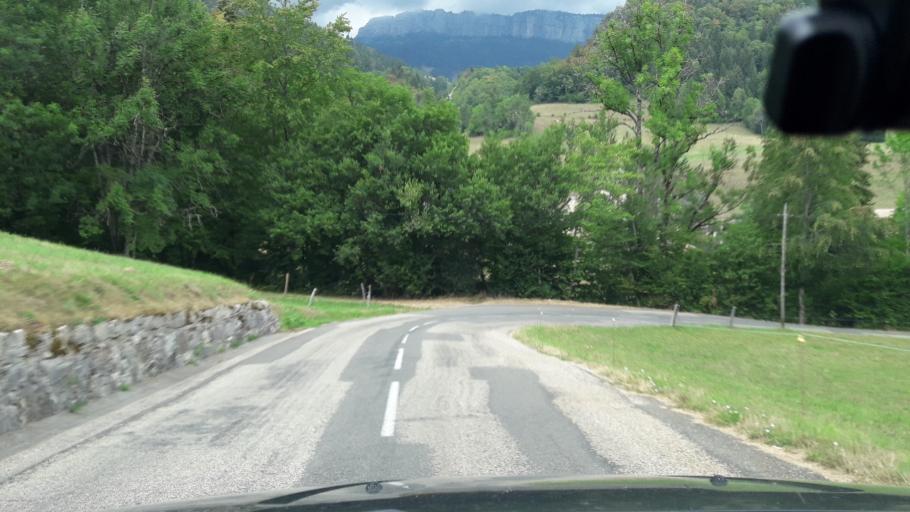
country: FR
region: Rhone-Alpes
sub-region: Departement de la Savoie
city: Vimines
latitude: 45.4507
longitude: 5.8776
